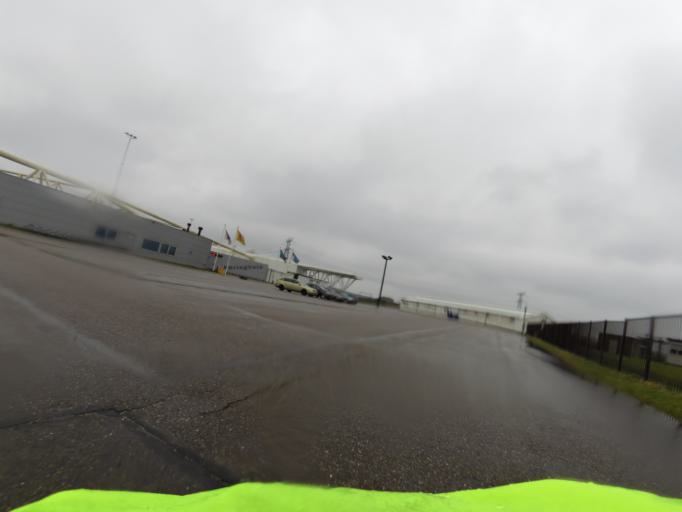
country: NL
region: South Holland
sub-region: Gemeente Rotterdam
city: Hoek van Holland
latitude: 51.9564
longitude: 4.1677
